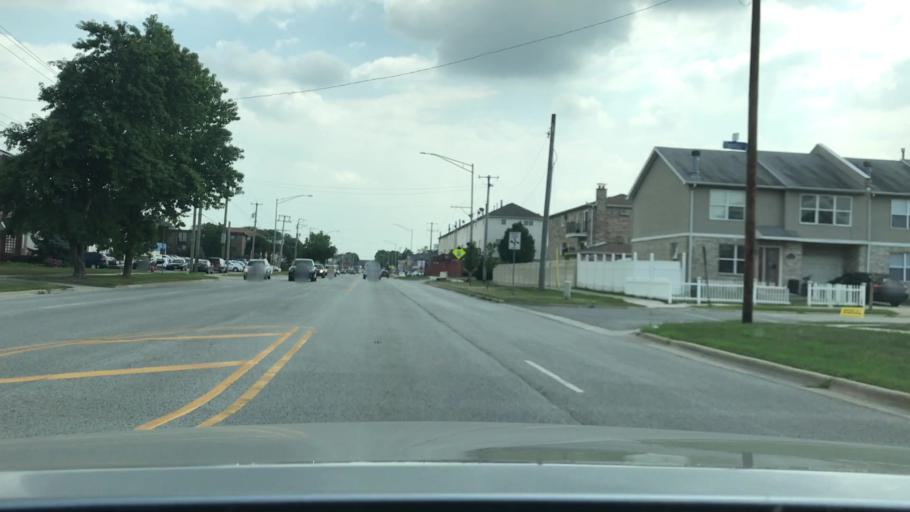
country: US
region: Illinois
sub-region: Cook County
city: Bridgeview
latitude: 41.7429
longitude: -87.8190
